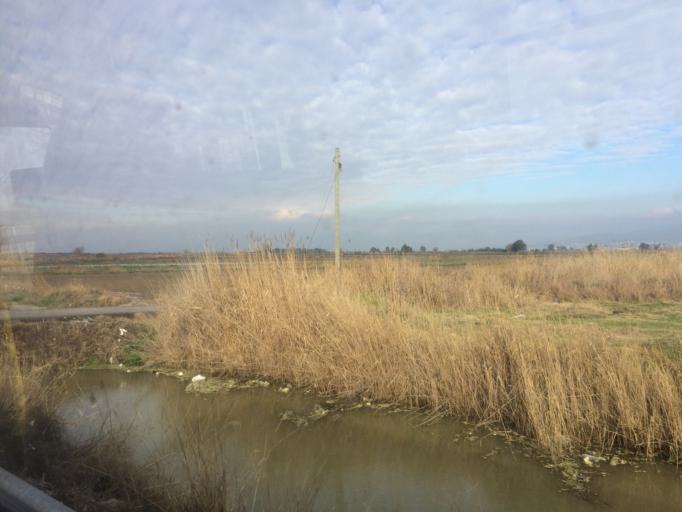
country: TR
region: Izmir
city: Menemen
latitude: 38.5076
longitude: 26.9582
